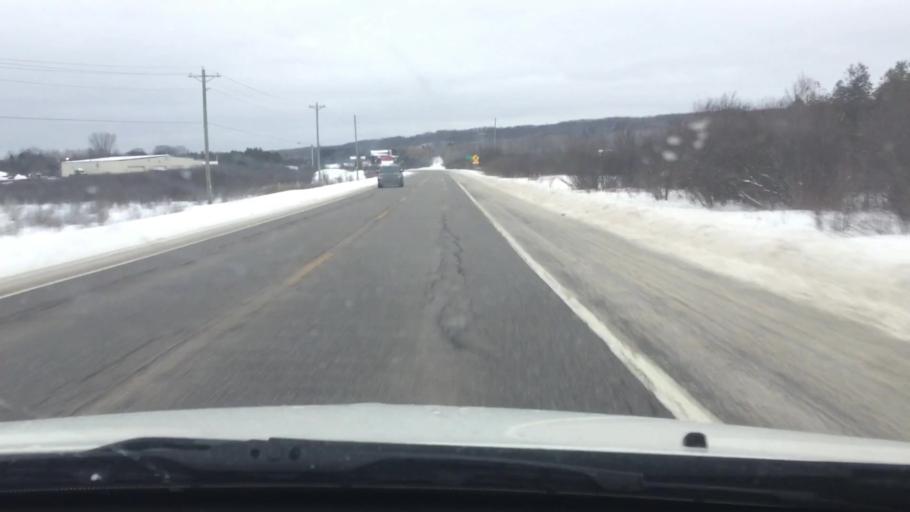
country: US
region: Michigan
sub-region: Charlevoix County
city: East Jordan
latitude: 45.1360
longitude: -85.1398
